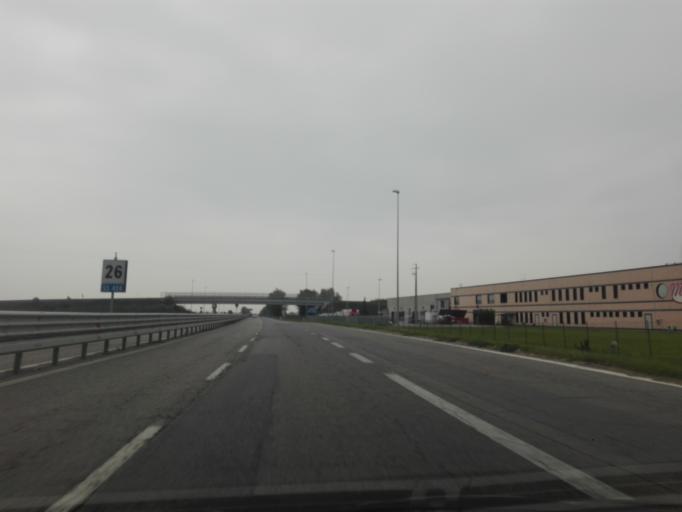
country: IT
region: Veneto
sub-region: Provincia di Verona
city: Roverchiara
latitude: 45.2714
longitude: 11.2212
